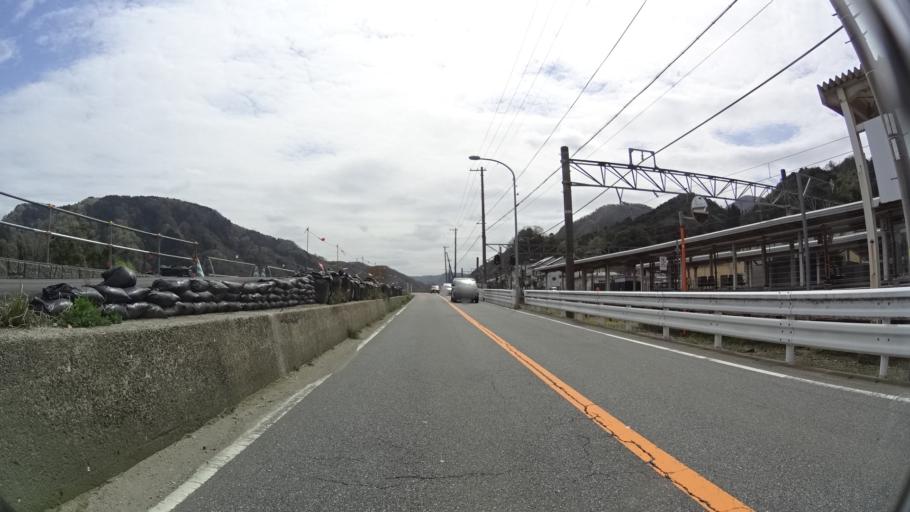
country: JP
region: Hyogo
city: Toyooka
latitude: 35.6127
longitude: 134.8051
